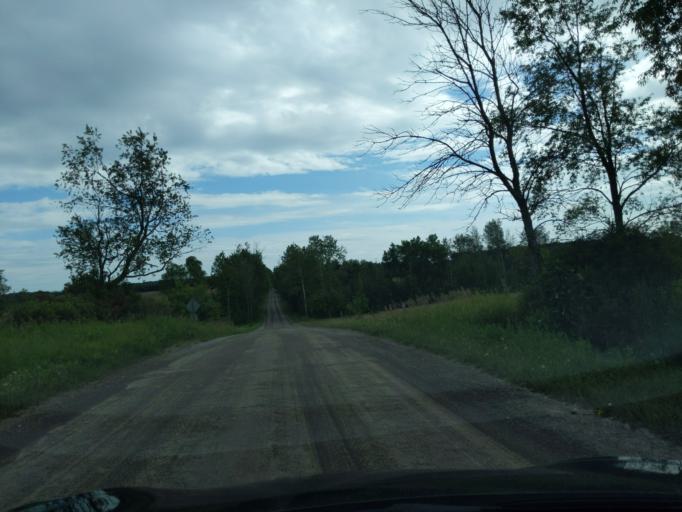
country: US
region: Michigan
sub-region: Clare County
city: Harrison
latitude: 43.9871
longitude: -84.9983
